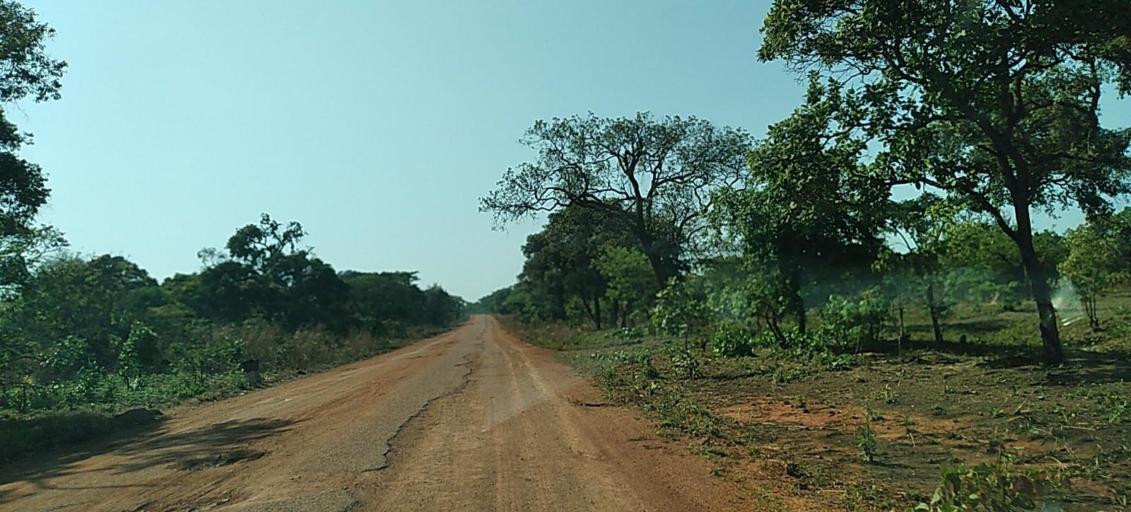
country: ZM
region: North-Western
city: Mwinilunga
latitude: -11.8953
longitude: 25.2716
